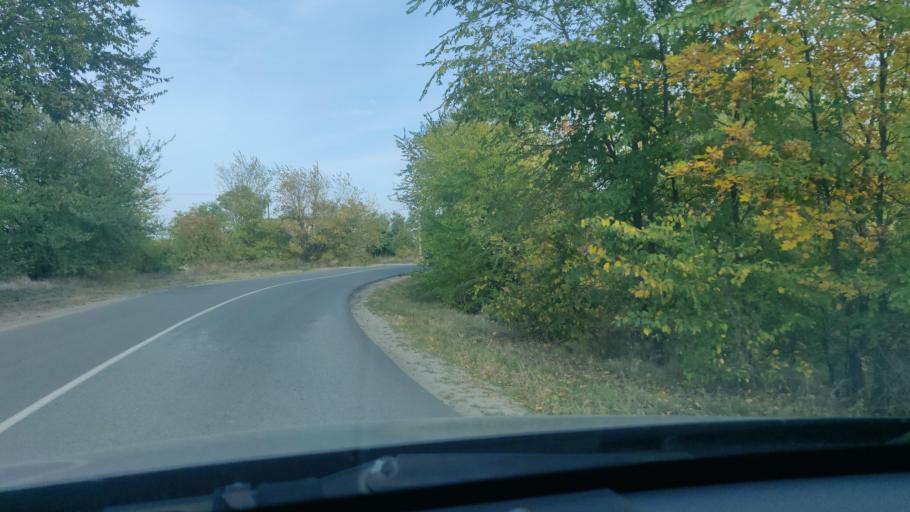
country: RU
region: Rostov
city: Ust'-Donetskiy
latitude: 47.6559
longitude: 40.8998
